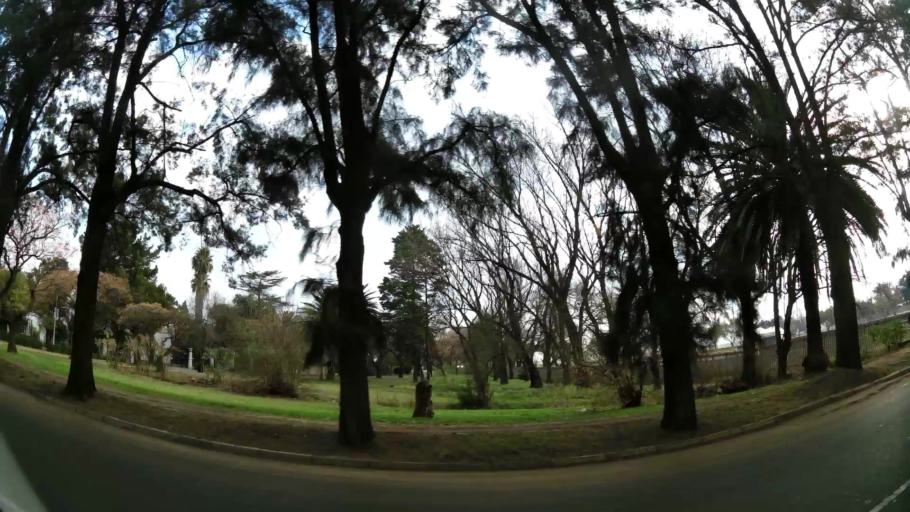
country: ZA
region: Gauteng
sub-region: Ekurhuleni Metropolitan Municipality
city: Germiston
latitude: -26.2295
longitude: 28.1722
